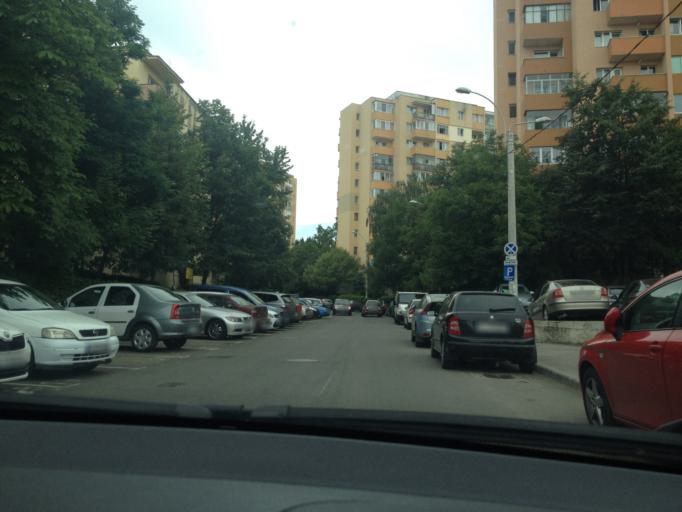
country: RO
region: Cluj
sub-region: Municipiul Cluj-Napoca
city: Cluj-Napoca
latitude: 46.7533
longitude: 23.5513
